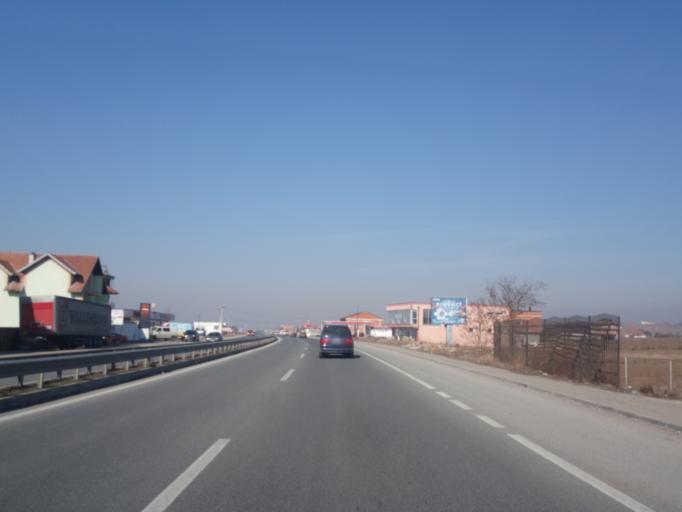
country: XK
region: Pristina
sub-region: Komuna e Obiliqit
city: Obiliq
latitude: 42.7457
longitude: 21.0472
